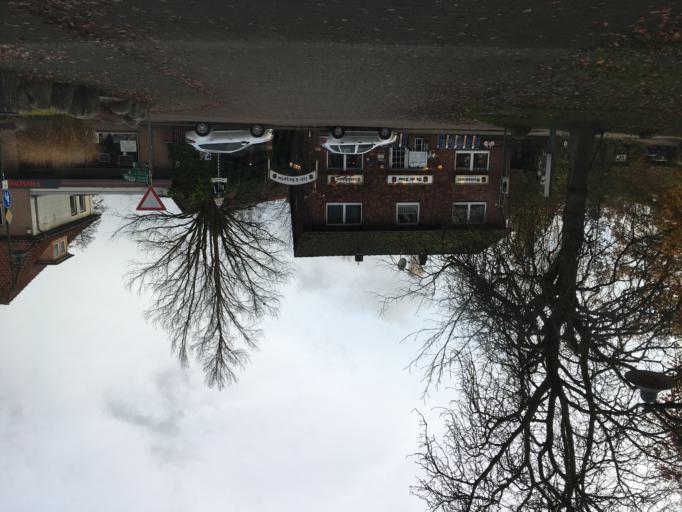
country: DE
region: Lower Saxony
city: Bispingen
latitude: 53.0822
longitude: 9.9973
